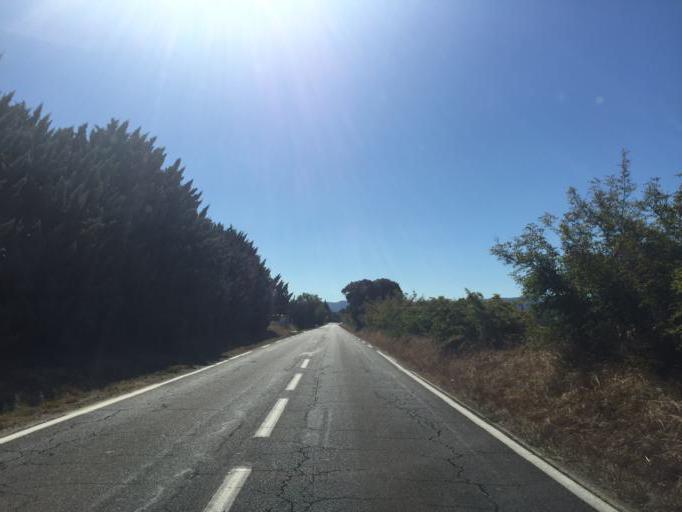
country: FR
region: Provence-Alpes-Cote d'Azur
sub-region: Departement du Vaucluse
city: Carpentras
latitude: 44.0314
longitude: 5.0803
